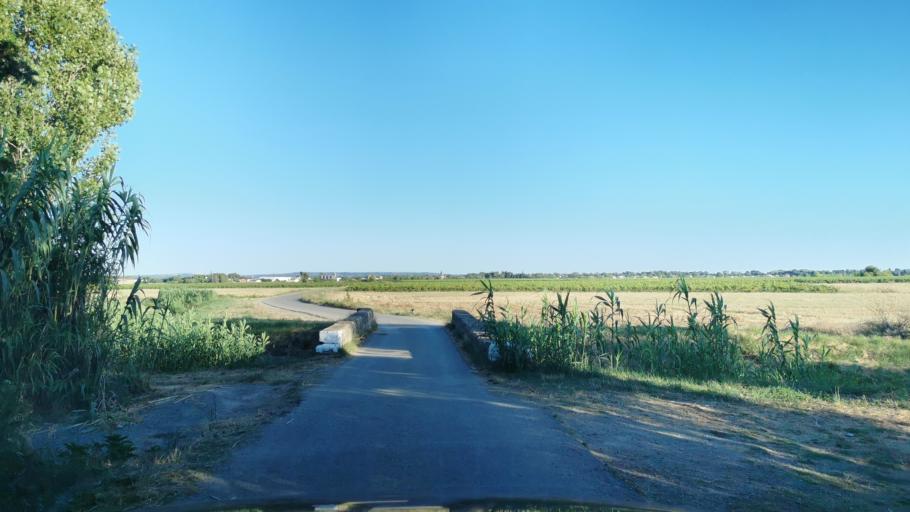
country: FR
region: Languedoc-Roussillon
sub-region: Departement de l'Aude
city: Ouveillan
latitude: 43.2605
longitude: 2.9867
